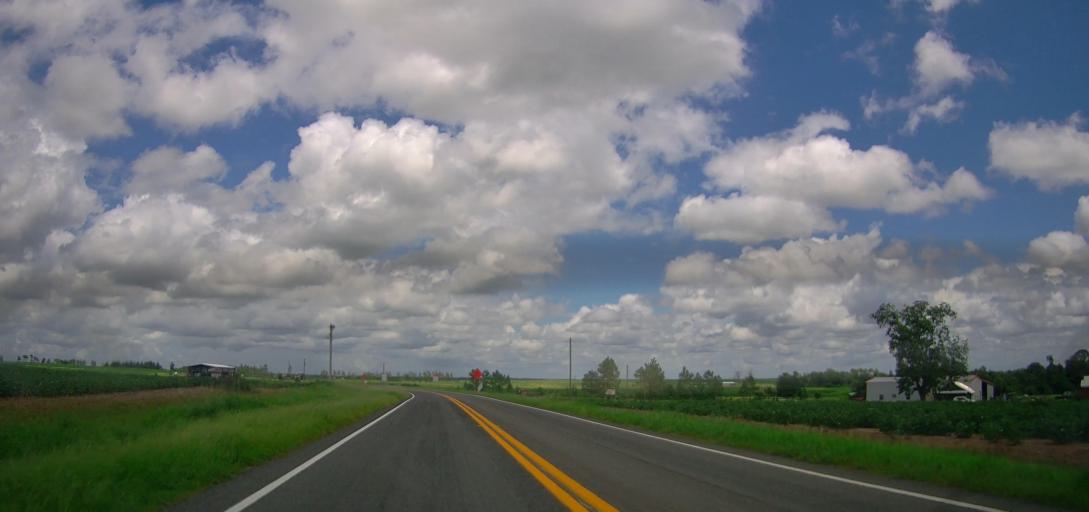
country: US
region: Georgia
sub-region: Turner County
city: Ashburn
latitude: 31.8205
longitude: -83.5652
